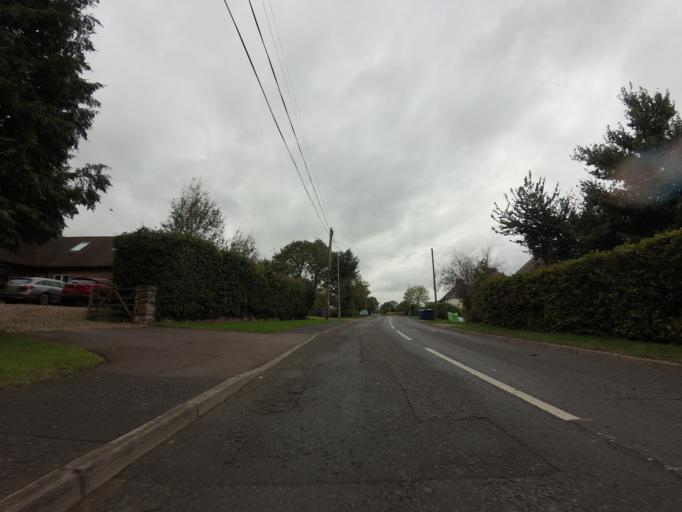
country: GB
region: England
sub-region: Cambridgeshire
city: Comberton
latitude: 52.1521
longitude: 0.0193
